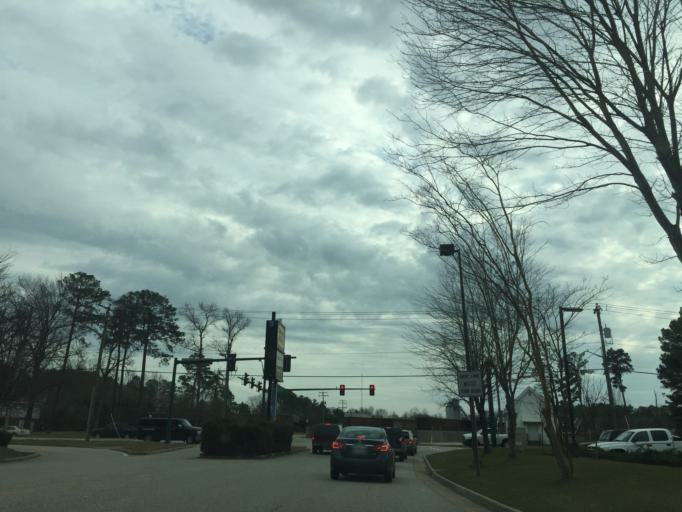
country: US
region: Virginia
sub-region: York County
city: Yorktown
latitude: 37.1059
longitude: -76.4981
